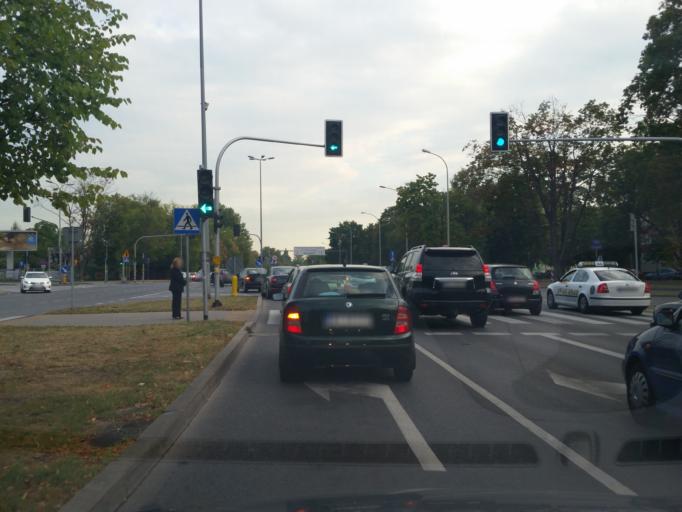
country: PL
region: Masovian Voivodeship
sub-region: Warszawa
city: Wlochy
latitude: 52.1804
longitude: 20.9780
